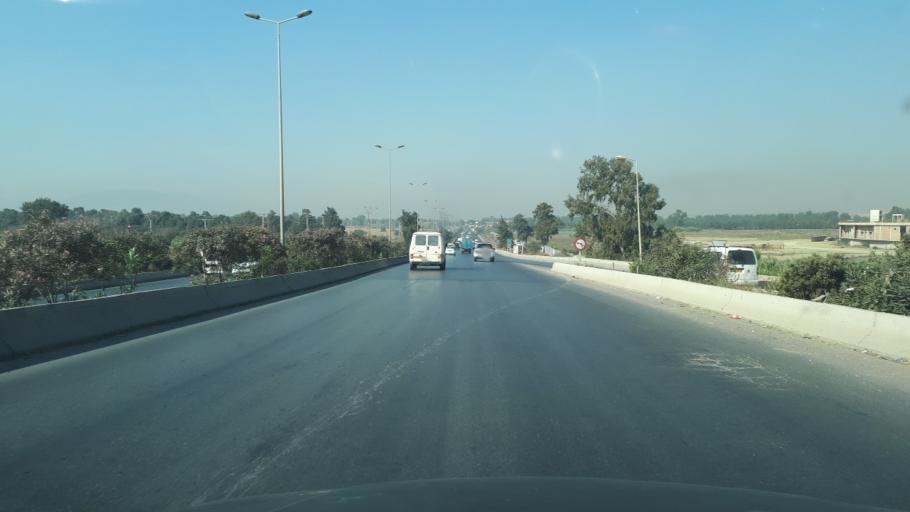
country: DZ
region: Tipaza
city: Baraki
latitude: 36.6928
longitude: 3.1255
